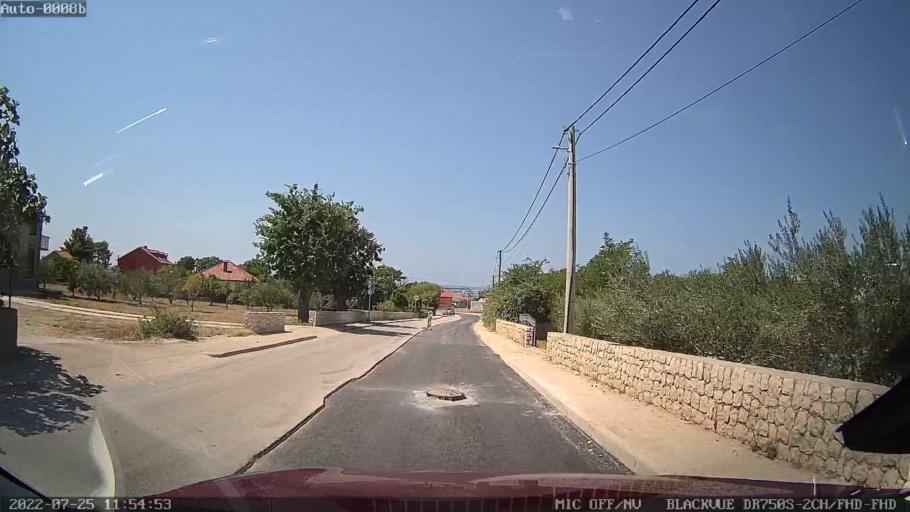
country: HR
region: Zadarska
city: Vrsi
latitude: 44.2589
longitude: 15.2301
